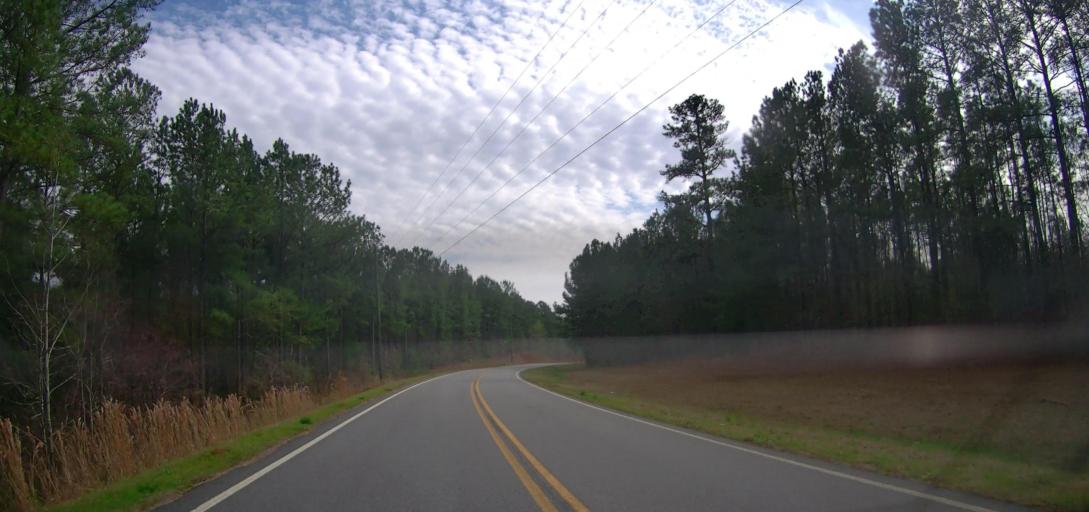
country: US
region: Georgia
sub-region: Jones County
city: Gray
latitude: 33.0596
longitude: -83.7242
